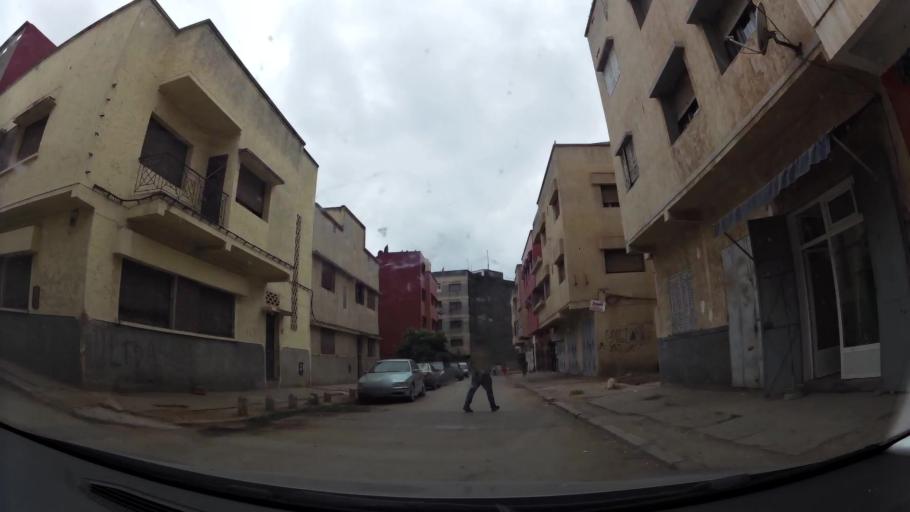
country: MA
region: Rabat-Sale-Zemmour-Zaer
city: Sale
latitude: 34.0381
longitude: -6.8054
